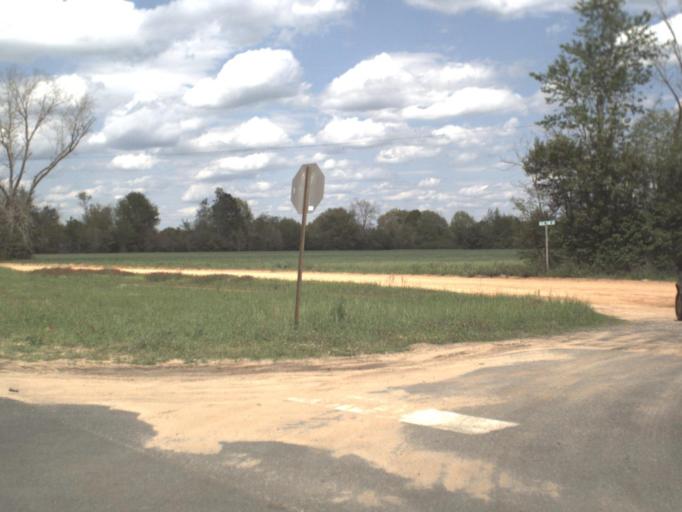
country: US
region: Florida
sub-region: Okaloosa County
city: Crestview
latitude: 30.8620
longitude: -86.5270
